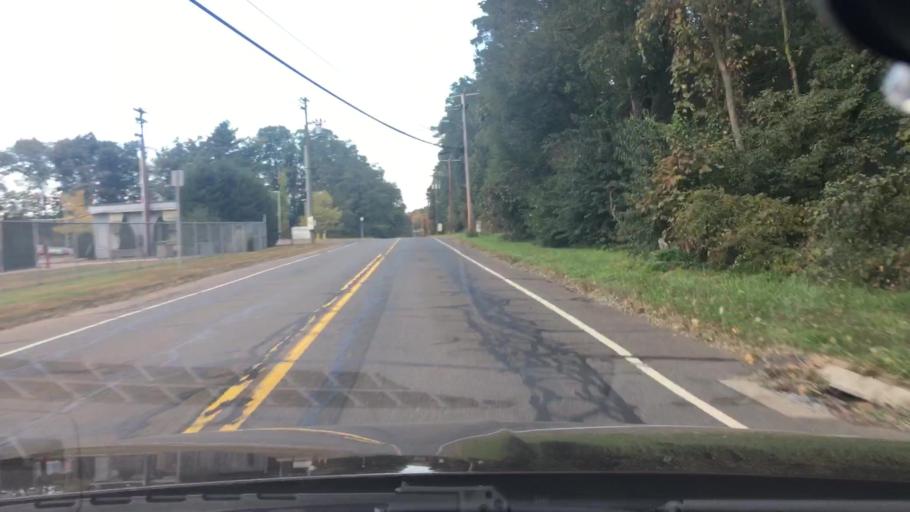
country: US
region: Connecticut
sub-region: Hartford County
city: South Windsor
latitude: 41.8341
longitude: -72.6085
